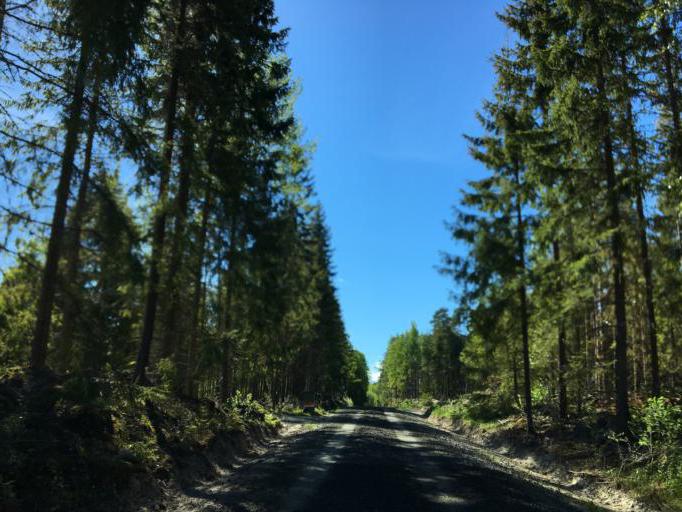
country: SE
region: Soedermanland
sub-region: Eskilstuna Kommun
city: Hallbybrunn
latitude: 59.3548
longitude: 16.3522
